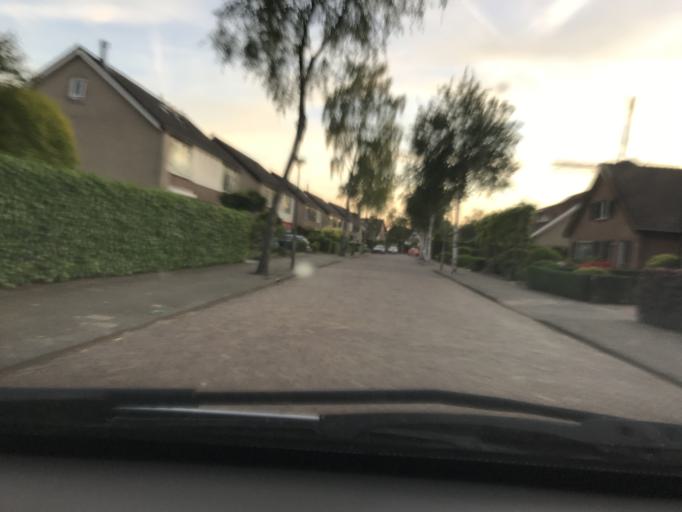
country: NL
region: North Brabant
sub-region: Gemeente Breda
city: Breda
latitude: 51.5458
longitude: 4.8000
